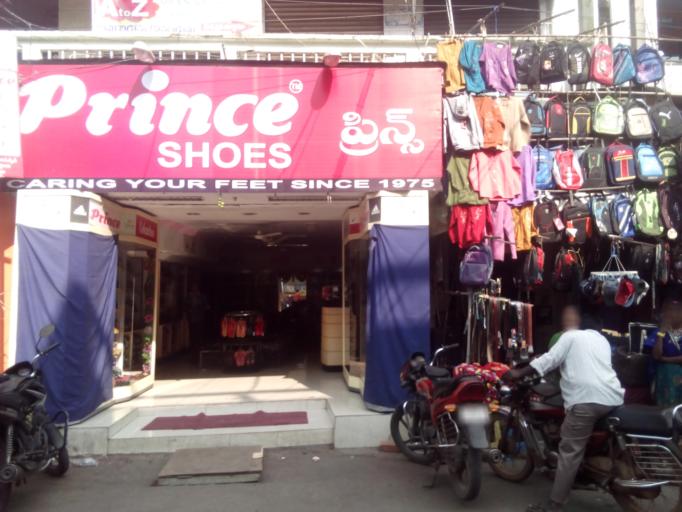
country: IN
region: Andhra Pradesh
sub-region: East Godavari
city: Rajahmundry
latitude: 16.9971
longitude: 81.7733
